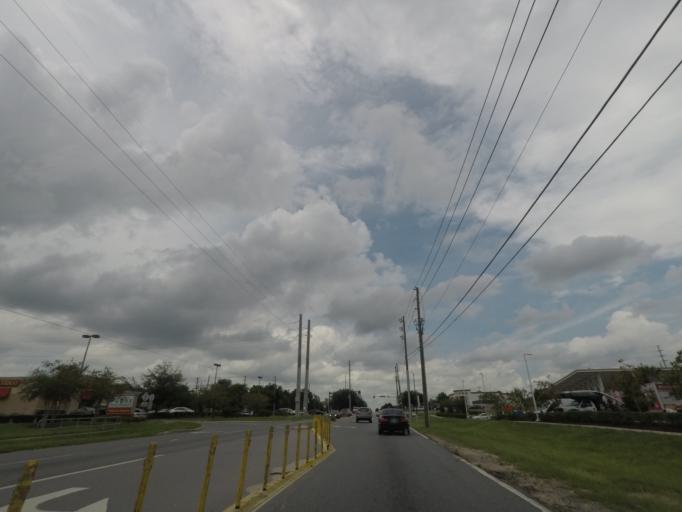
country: US
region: Florida
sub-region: Polk County
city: Loughman
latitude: 28.2585
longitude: -81.5906
